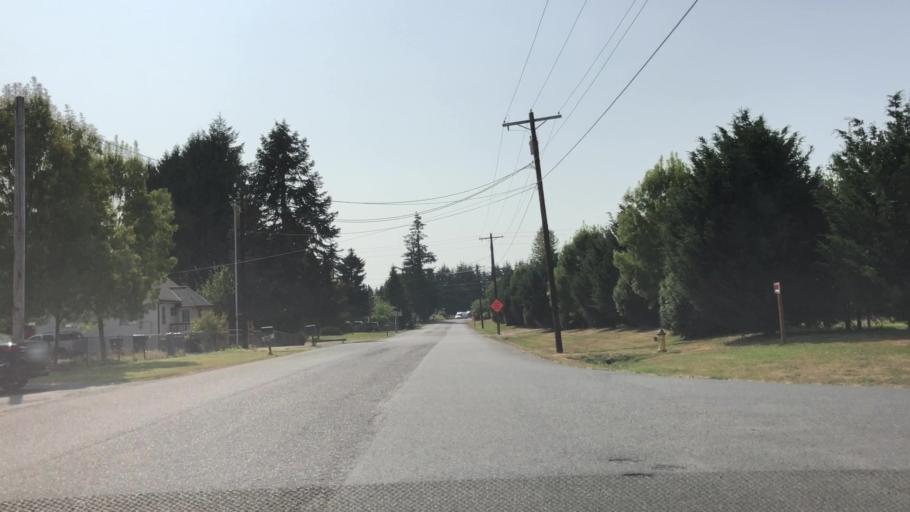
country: US
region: Washington
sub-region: Snohomish County
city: Lochsloy
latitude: 48.0540
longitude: -122.0267
